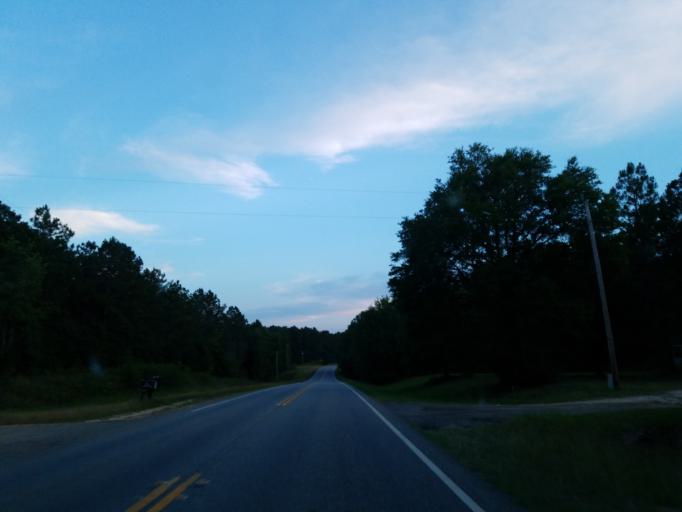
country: US
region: Georgia
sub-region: Worth County
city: Sylvester
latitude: 31.6653
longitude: -83.8080
